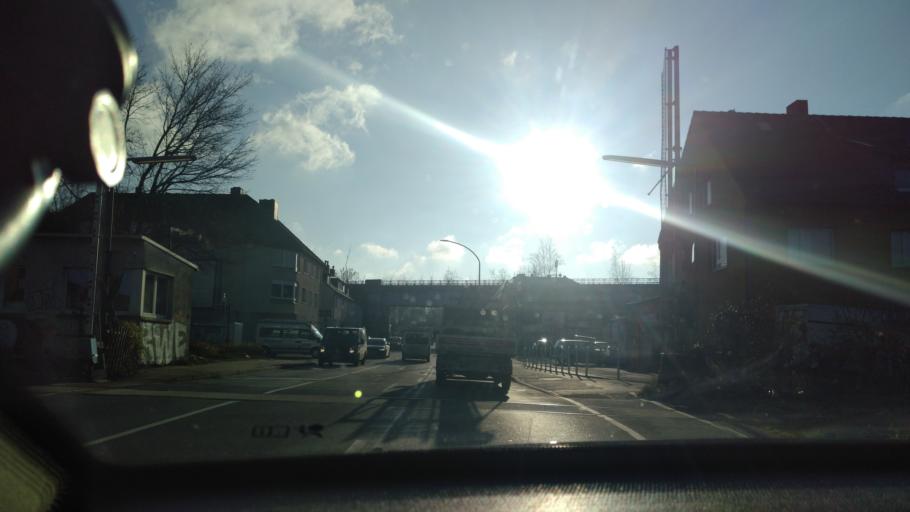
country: DE
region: North Rhine-Westphalia
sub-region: Regierungsbezirk Dusseldorf
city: Essen
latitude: 51.4846
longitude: 6.9794
